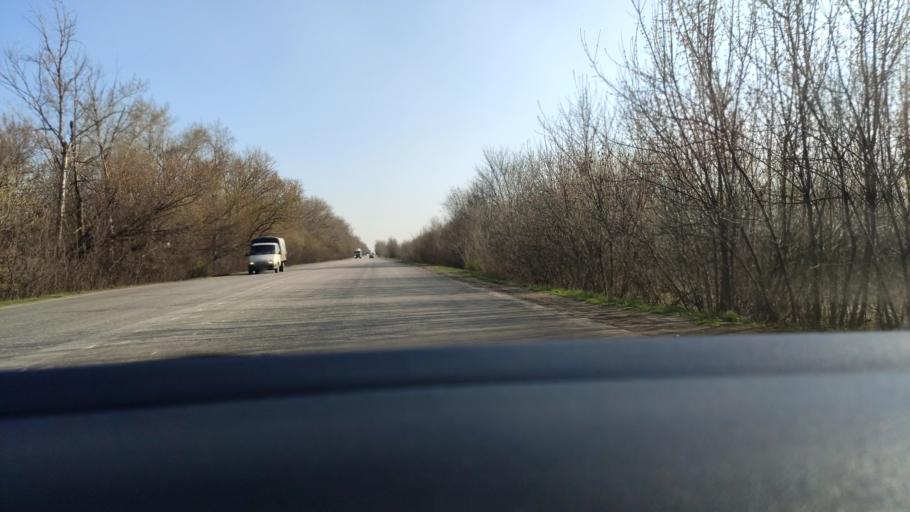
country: RU
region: Voronezj
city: Maslovka
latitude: 51.4913
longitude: 39.3080
